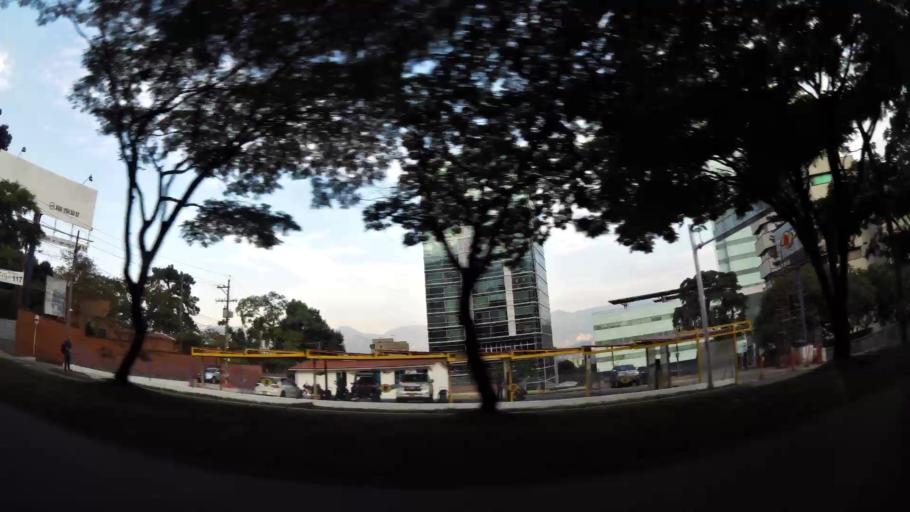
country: CO
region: Antioquia
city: Medellin
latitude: 6.2173
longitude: -75.5699
